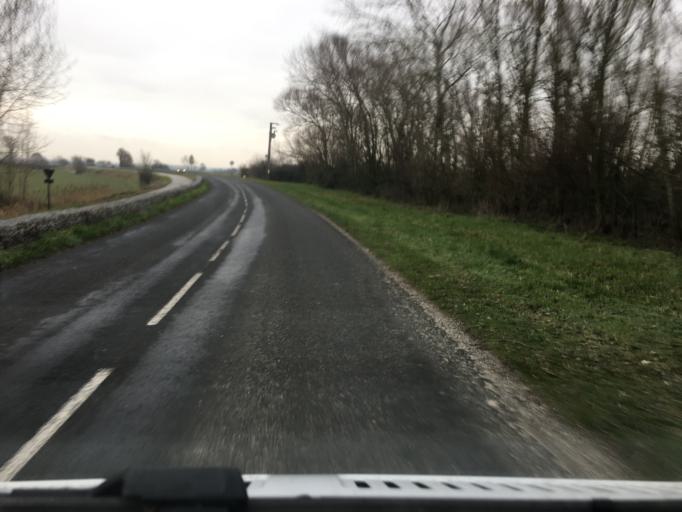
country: FR
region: Picardie
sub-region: Departement de la Somme
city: Pende
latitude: 50.2088
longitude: 1.5564
